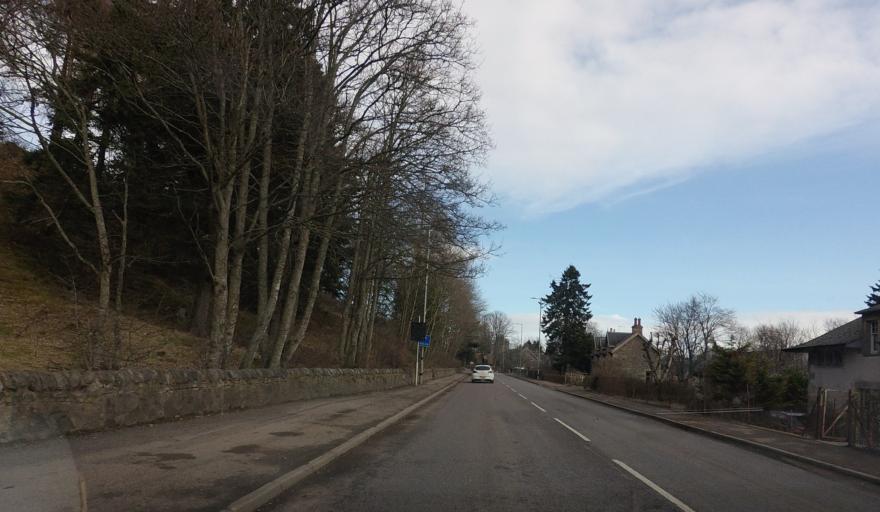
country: GB
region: Scotland
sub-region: Highland
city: Kingussie
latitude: 57.0786
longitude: -4.0580
